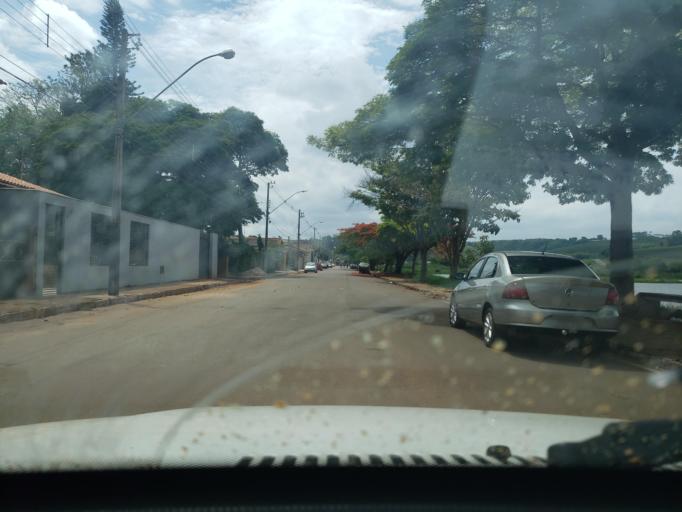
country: BR
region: Minas Gerais
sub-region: Boa Esperanca
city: Boa Esperanca
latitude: -21.0822
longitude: -45.5726
